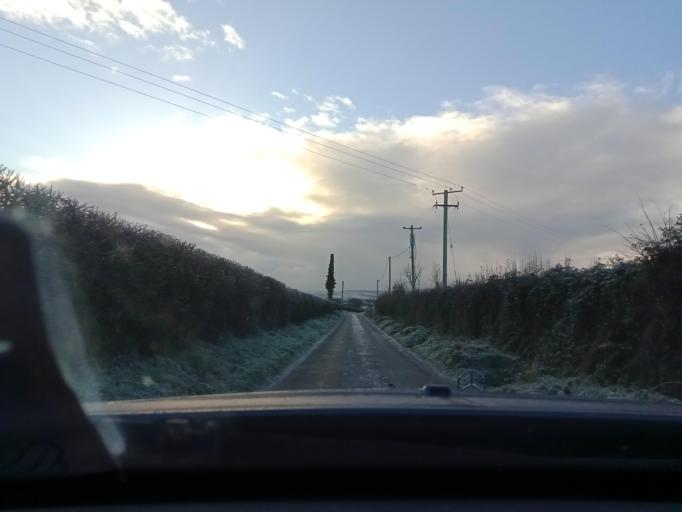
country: IE
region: Leinster
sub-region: County Carlow
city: Bagenalstown
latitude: 52.6342
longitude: -7.0156
